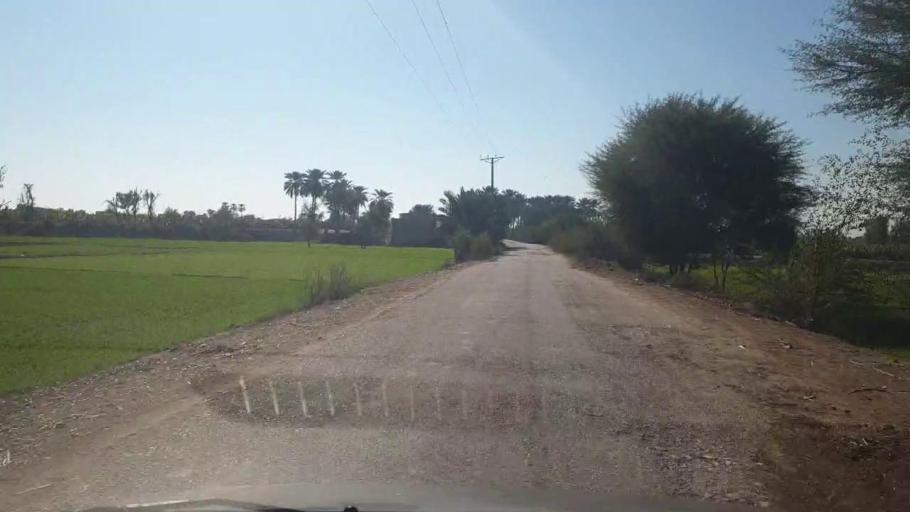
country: PK
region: Sindh
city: Bozdar
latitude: 27.2502
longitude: 68.6519
